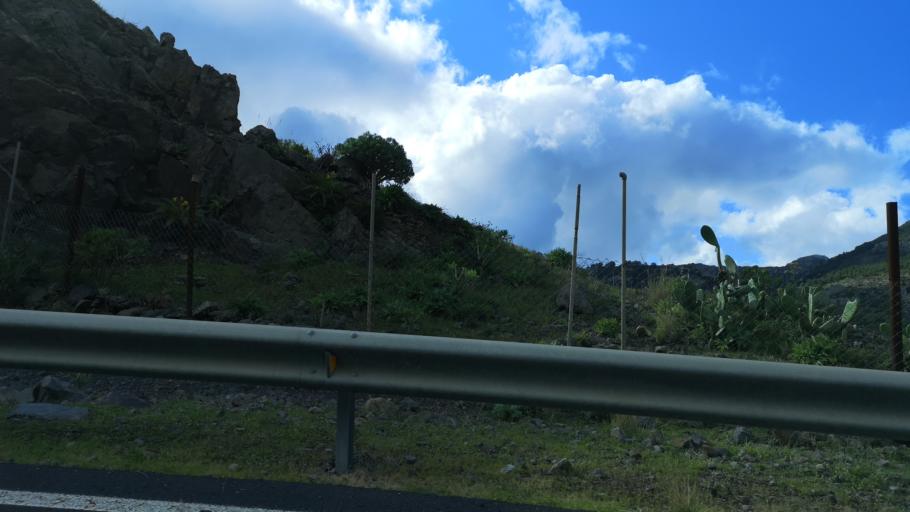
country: ES
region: Canary Islands
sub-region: Provincia de Santa Cruz de Tenerife
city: Alajero
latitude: 28.0935
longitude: -17.1955
